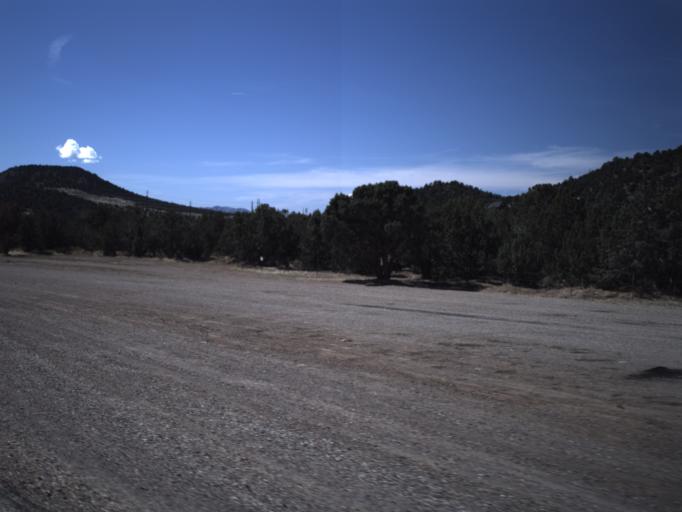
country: US
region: Utah
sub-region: Washington County
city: Enterprise
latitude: 37.4229
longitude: -113.6307
